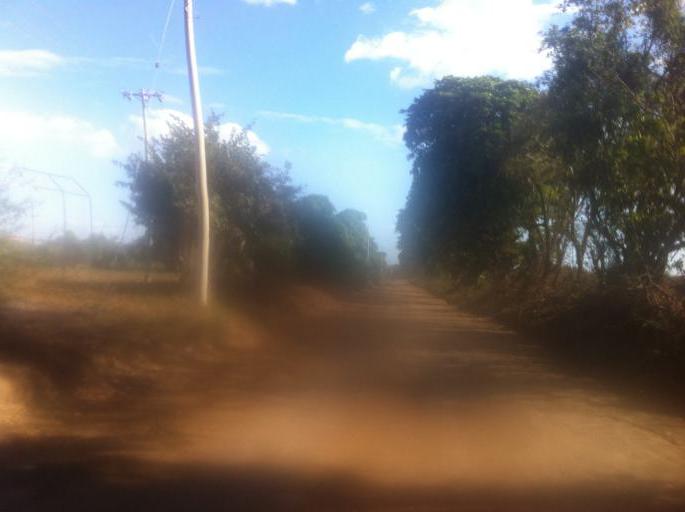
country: NI
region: Managua
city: Carlos Fonseca Amador
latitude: 11.8956
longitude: -86.5867
